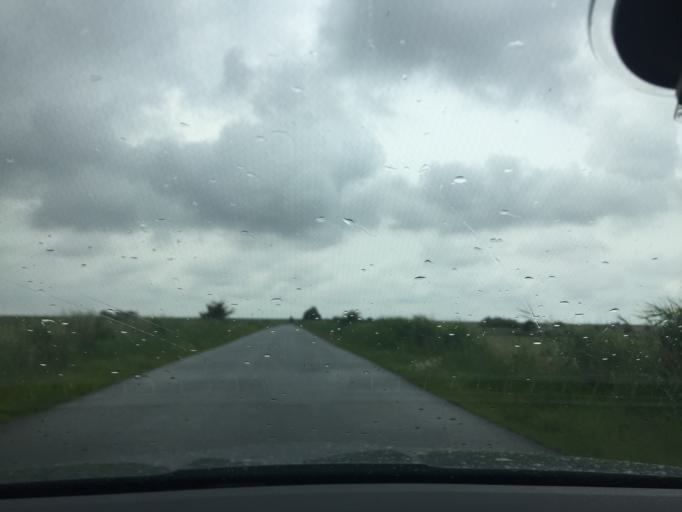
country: DE
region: Lower Saxony
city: Wirdum
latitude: 53.4962
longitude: 7.0641
